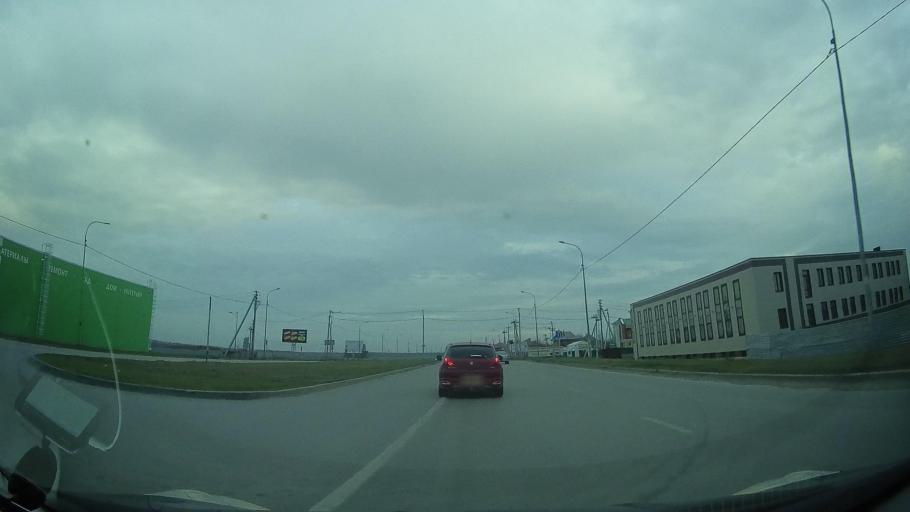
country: RU
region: Rostov
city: Temernik
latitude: 47.3089
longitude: 39.7276
